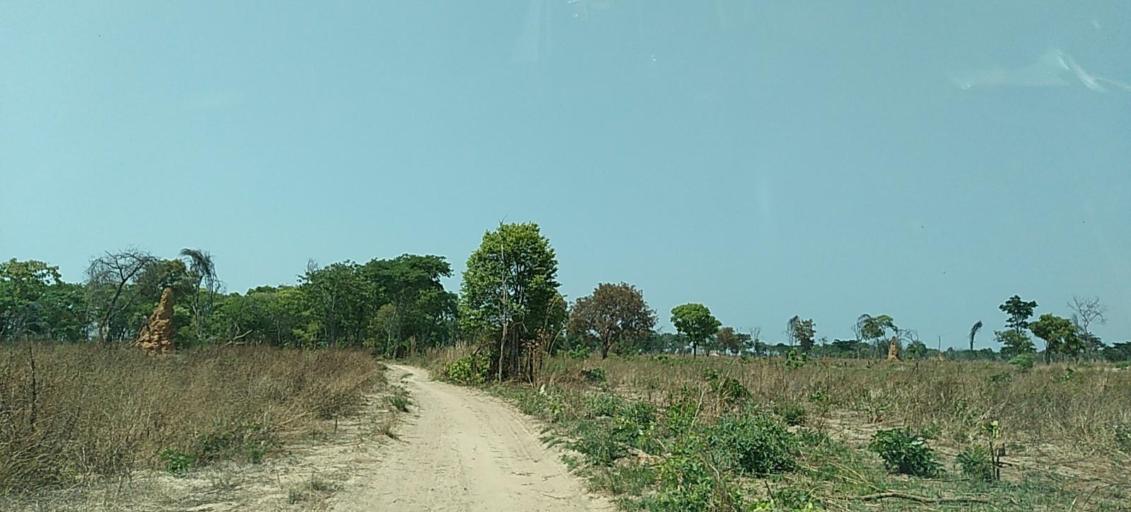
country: ZM
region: Copperbelt
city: Mpongwe
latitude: -13.8653
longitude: 28.0539
